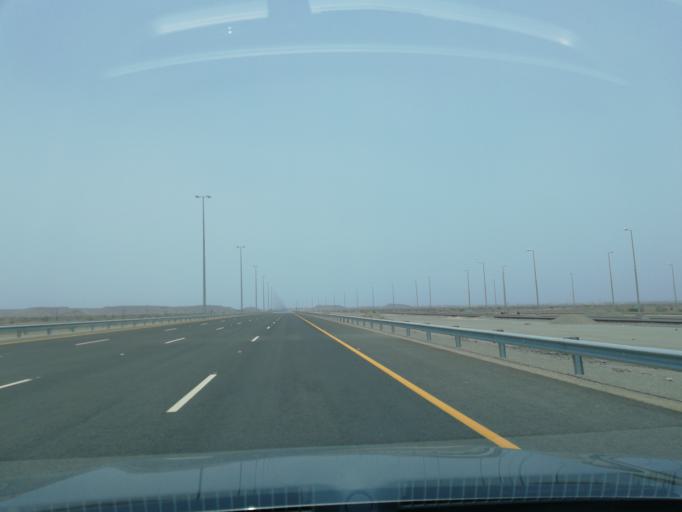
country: OM
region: Al Batinah
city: Al Liwa'
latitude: 24.4841
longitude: 56.5071
